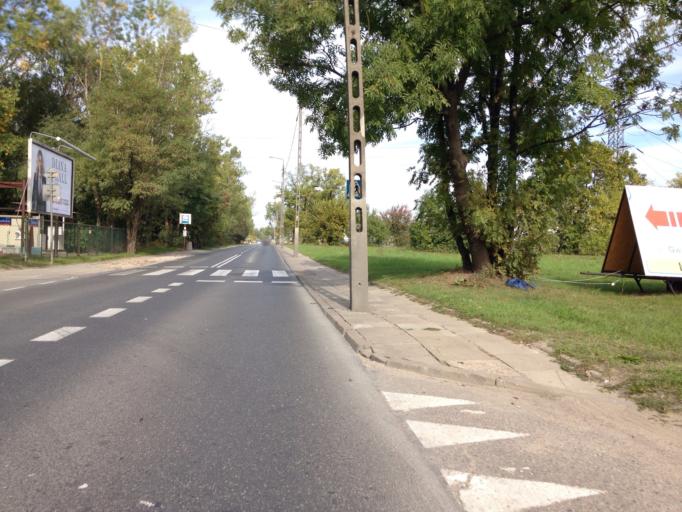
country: PL
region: Masovian Voivodeship
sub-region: Powiat wolominski
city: Zabki
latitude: 52.2643
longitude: 21.1224
